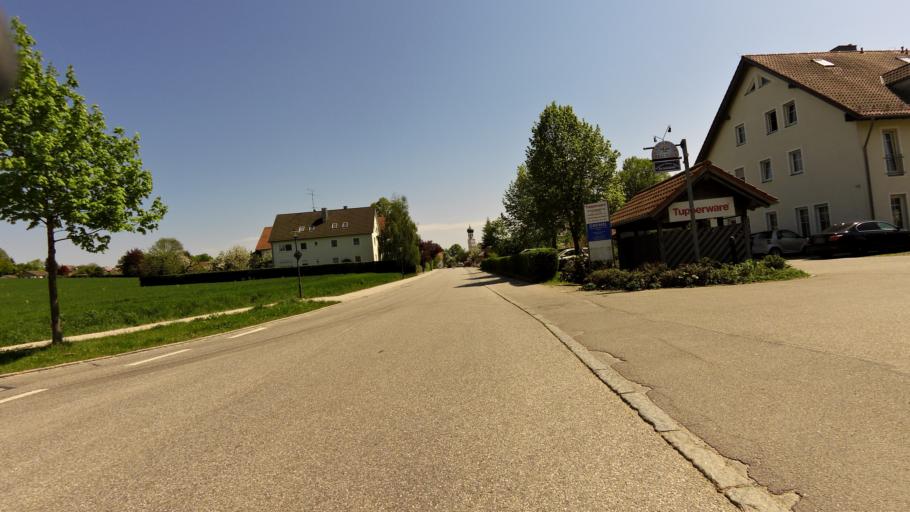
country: DE
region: Bavaria
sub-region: Lower Bavaria
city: Weihmichl
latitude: 48.5754
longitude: 12.0744
